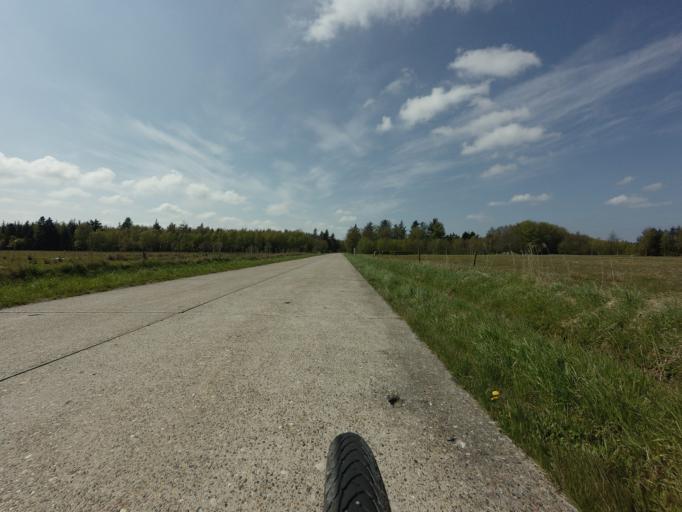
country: DK
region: North Denmark
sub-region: Jammerbugt Kommune
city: Brovst
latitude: 57.1644
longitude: 9.4889
